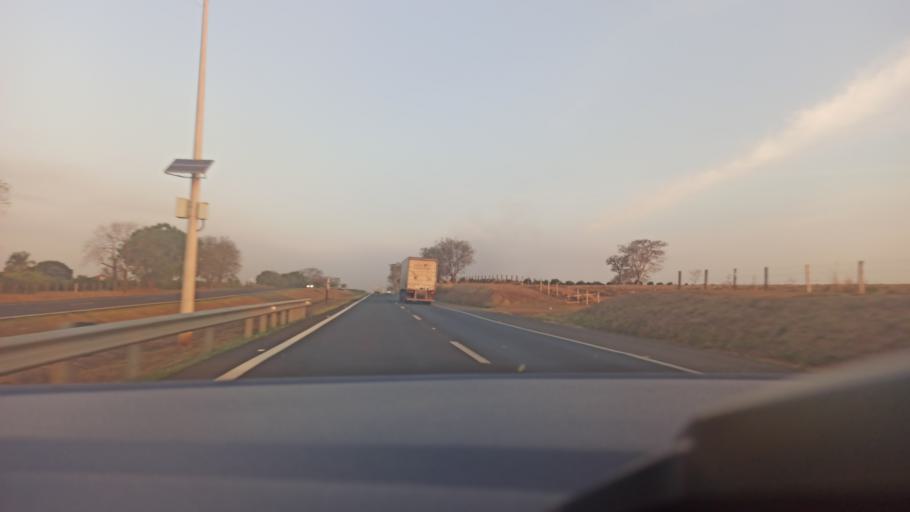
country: BR
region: Sao Paulo
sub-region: Taquaritinga
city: Taquaritinga
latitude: -21.4415
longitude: -48.6481
